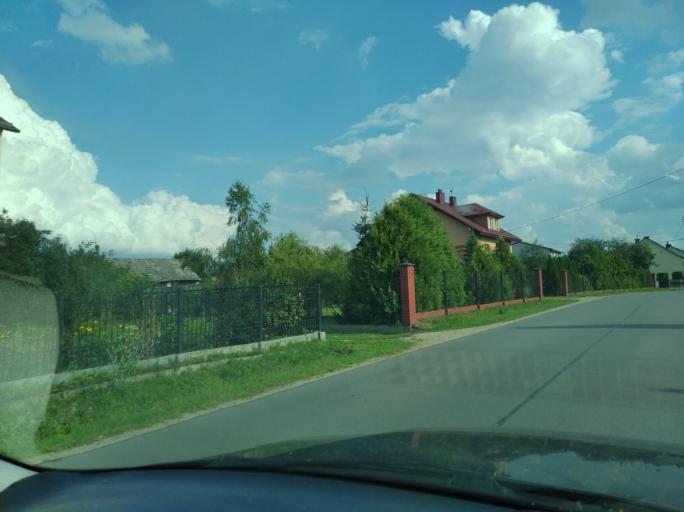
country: PL
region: Subcarpathian Voivodeship
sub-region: Powiat rzeszowski
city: Wysoka Glogowska
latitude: 50.1492
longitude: 22.0169
